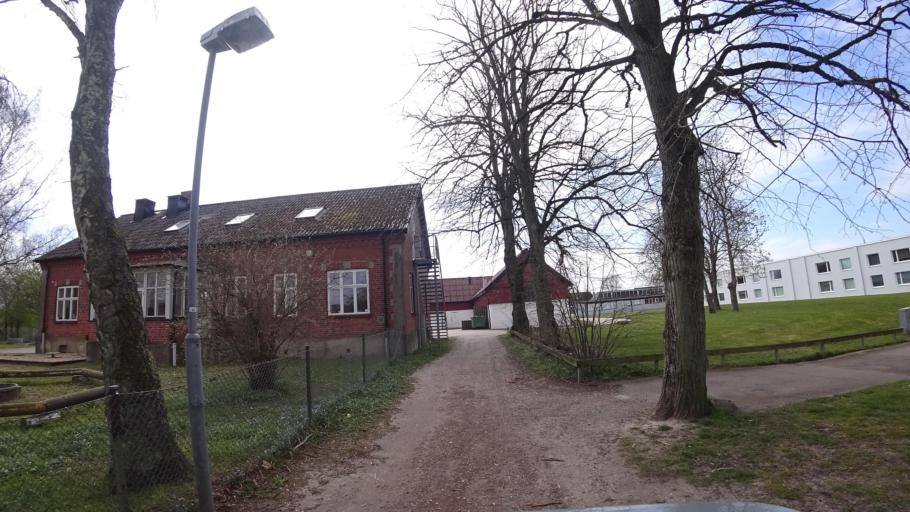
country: SE
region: Skane
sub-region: Staffanstorps Kommun
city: Staffanstorp
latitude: 55.6397
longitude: 13.2020
